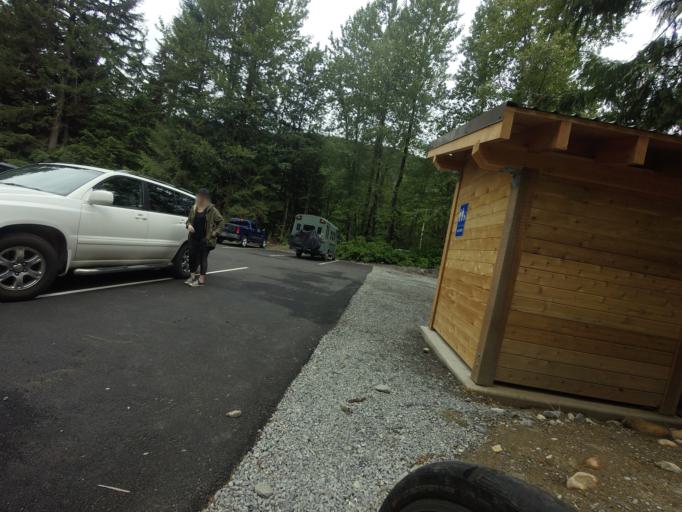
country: CA
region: British Columbia
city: Whistler
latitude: 50.0865
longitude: -123.0357
